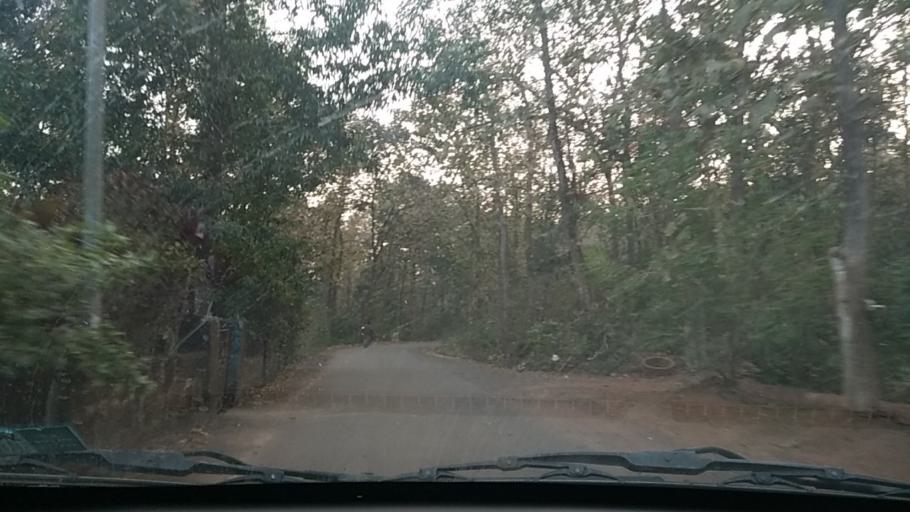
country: IN
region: Goa
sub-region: South Goa
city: Sancoale
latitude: 15.3515
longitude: 73.9371
